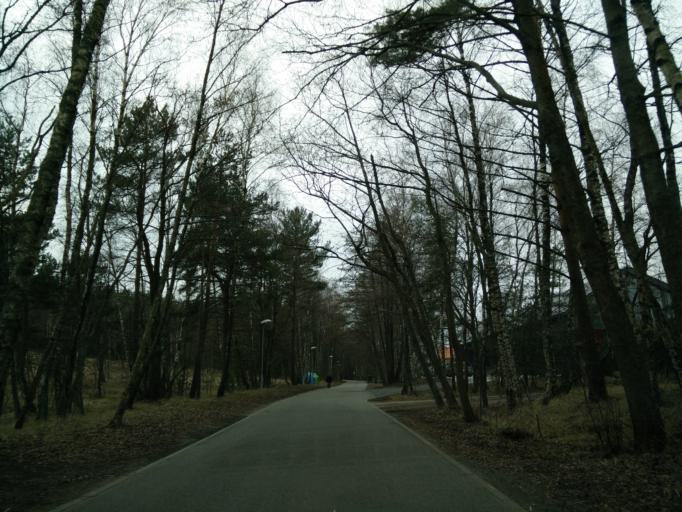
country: LT
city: Nida
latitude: 55.2999
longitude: 20.9877
